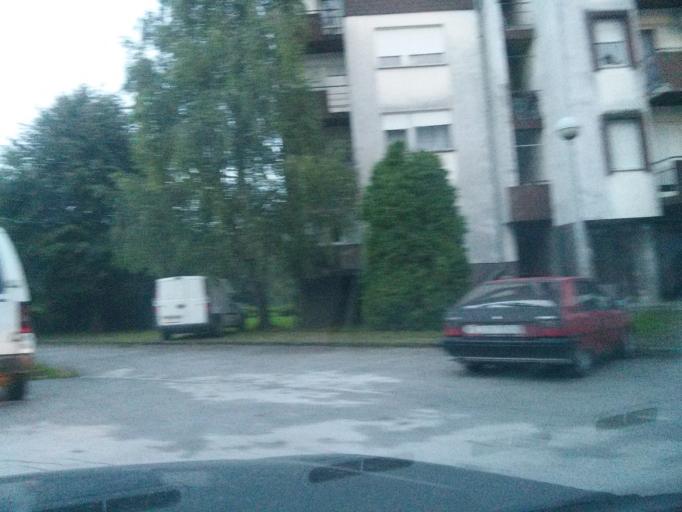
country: HR
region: Sisacko-Moslavacka
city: Gvozd
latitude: 45.2993
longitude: 15.9709
